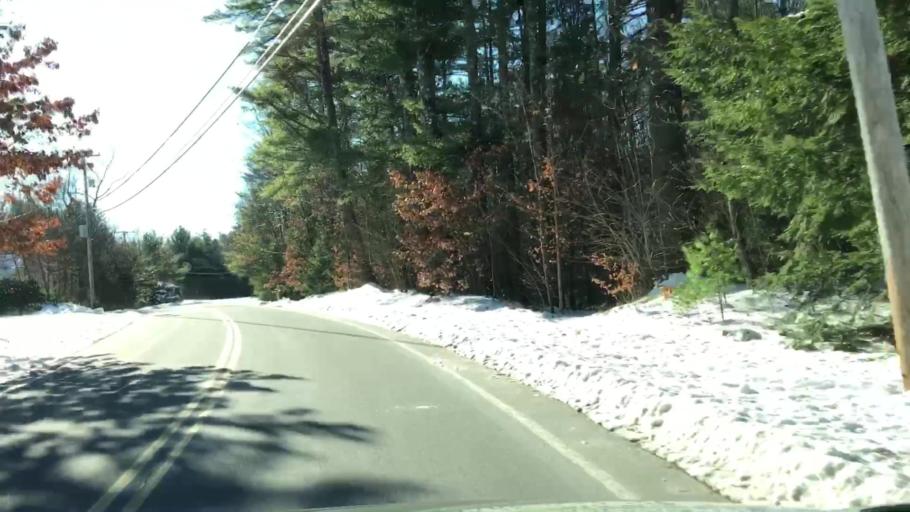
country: US
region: New Hampshire
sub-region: Hillsborough County
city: Bedford
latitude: 42.9337
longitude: -71.5514
